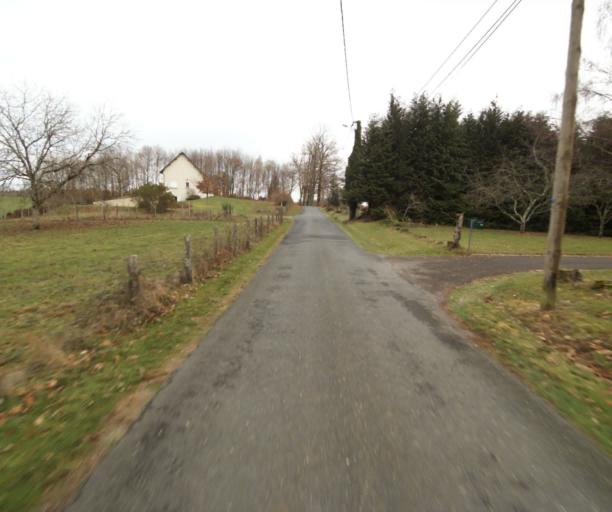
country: FR
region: Limousin
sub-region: Departement de la Correze
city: Chameyrat
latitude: 45.2360
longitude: 1.6780
